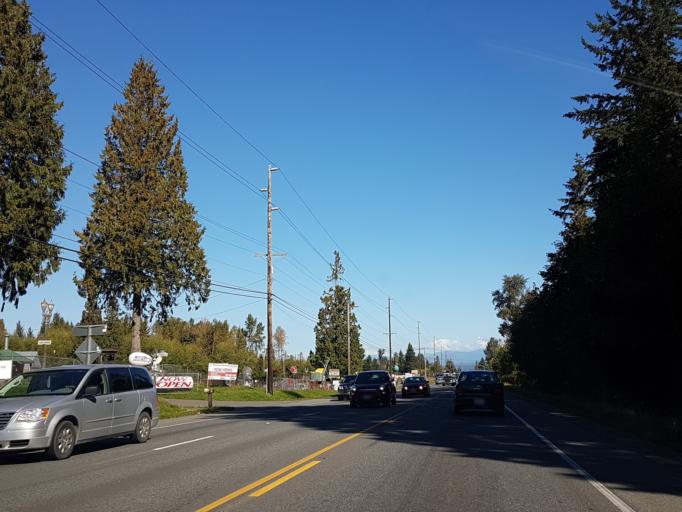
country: US
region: Washington
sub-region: Snohomish County
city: Clearview
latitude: 47.8423
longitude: -122.1211
